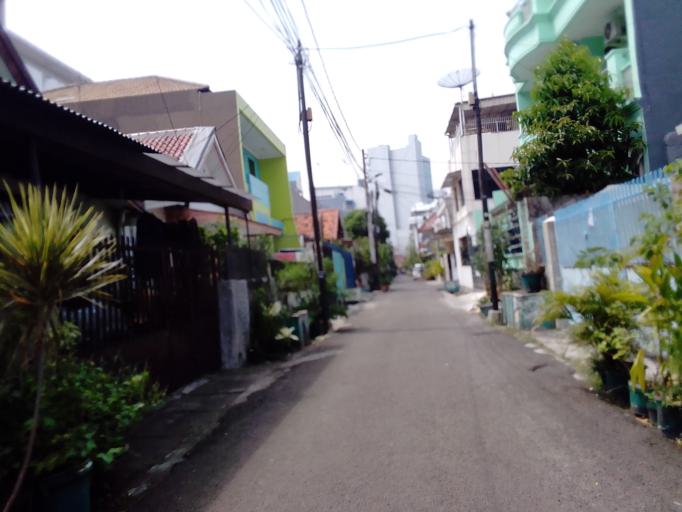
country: ID
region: Jakarta Raya
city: Jakarta
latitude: -6.1738
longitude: 106.8076
